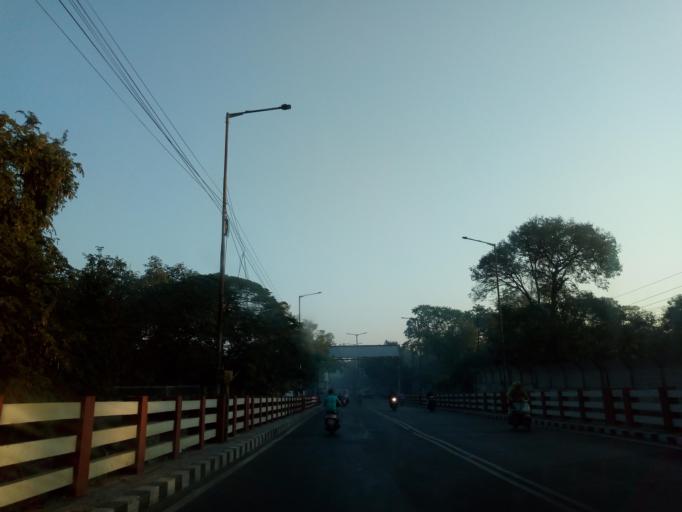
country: IN
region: Telangana
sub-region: Hyderabad
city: Malkajgiri
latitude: 17.4117
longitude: 78.5195
